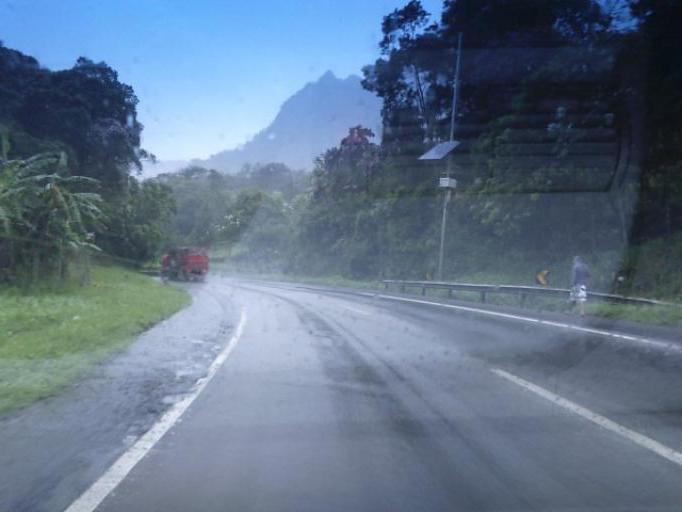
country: BR
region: Sao Paulo
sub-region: Cajati
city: Cajati
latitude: -24.8799
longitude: -48.2094
